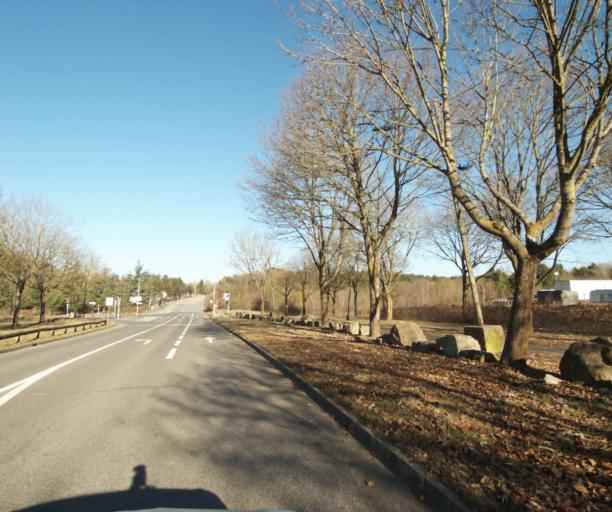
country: FR
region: Lorraine
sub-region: Departement de Meurthe-et-Moselle
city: Maxeville
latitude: 48.7099
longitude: 6.1482
